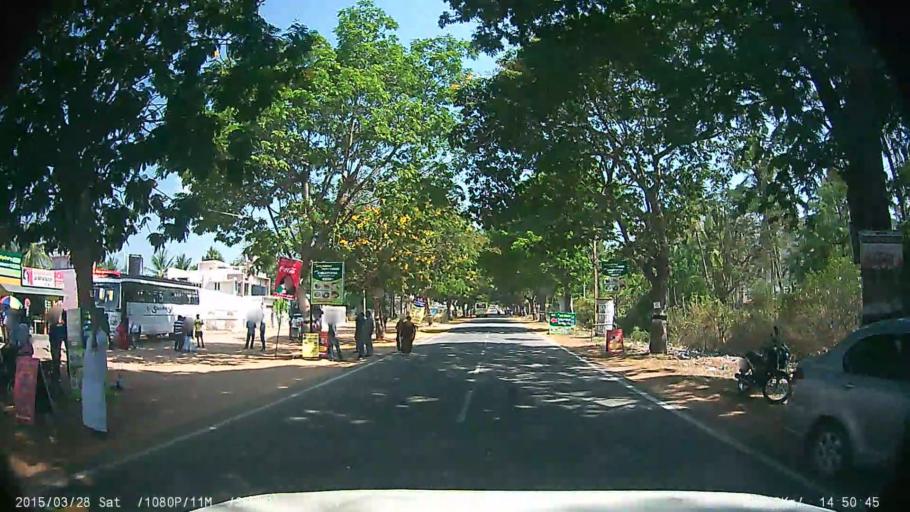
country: IN
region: Karnataka
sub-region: Mysore
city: Mysore
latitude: 12.2942
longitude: 76.6822
